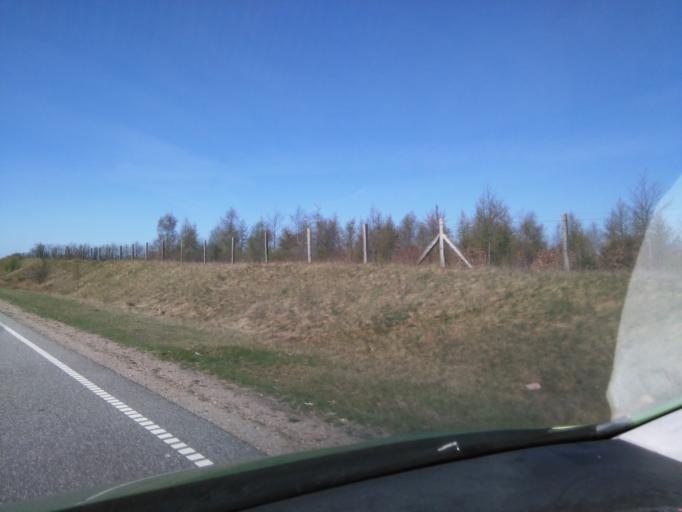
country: DK
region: South Denmark
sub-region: Vejle Kommune
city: Give
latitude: 55.8016
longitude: 9.2150
